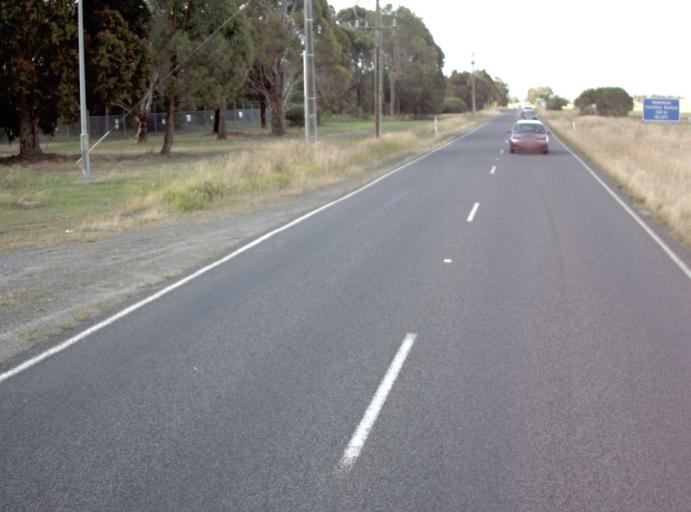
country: AU
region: Victoria
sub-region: Latrobe
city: Morwell
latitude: -38.2829
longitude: 146.4311
